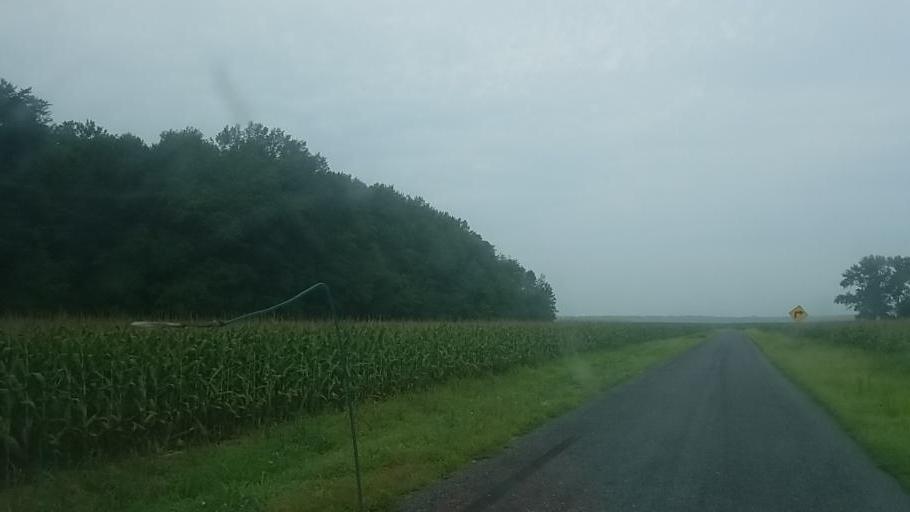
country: US
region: Delaware
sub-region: Sussex County
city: Selbyville
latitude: 38.4374
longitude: -75.2892
